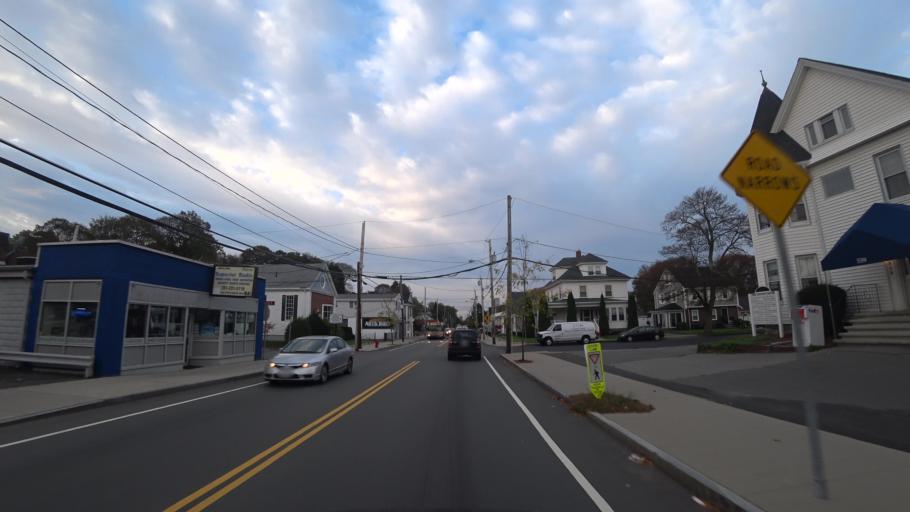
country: US
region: Massachusetts
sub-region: Essex County
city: Saugus
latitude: 42.4481
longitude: -71.0100
